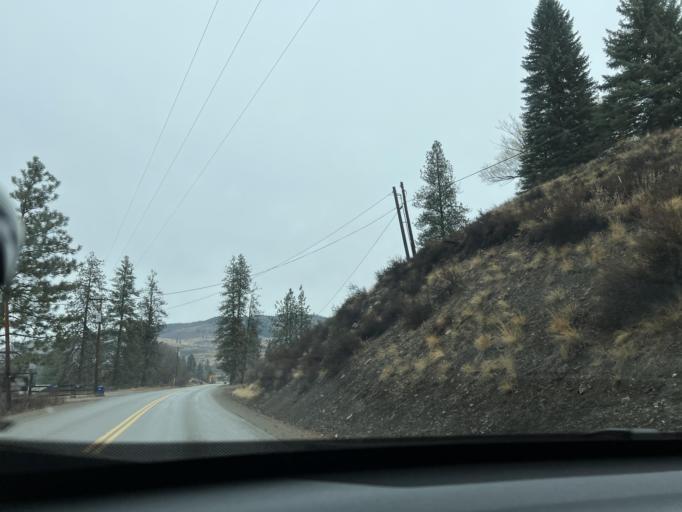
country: US
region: Washington
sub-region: Okanogan County
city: Brewster
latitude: 48.4931
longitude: -120.1783
